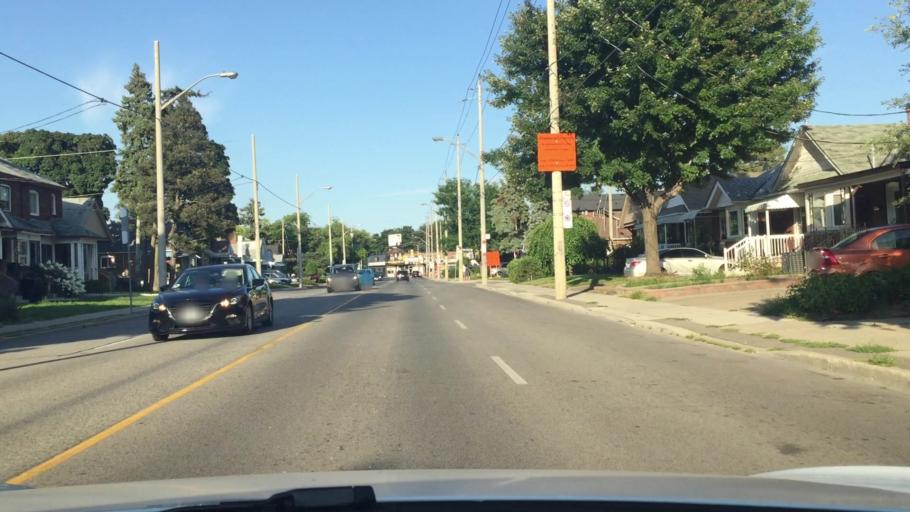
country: CA
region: Ontario
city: Toronto
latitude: 43.6941
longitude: -79.3460
